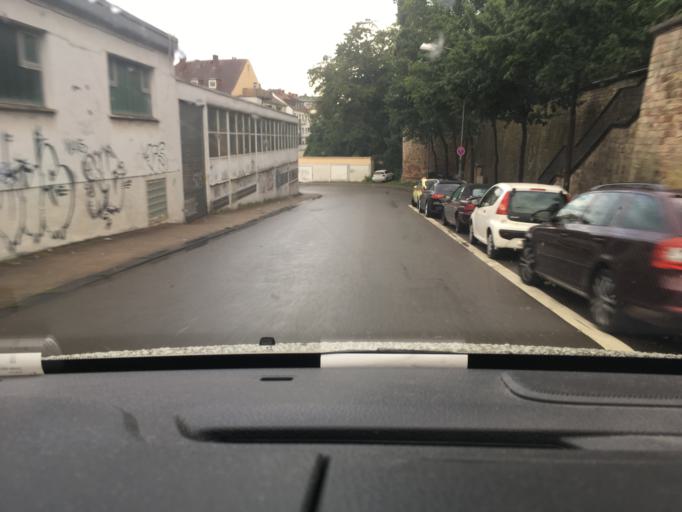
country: DE
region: Saarland
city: Saarbrucken
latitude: 49.2316
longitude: 6.9745
